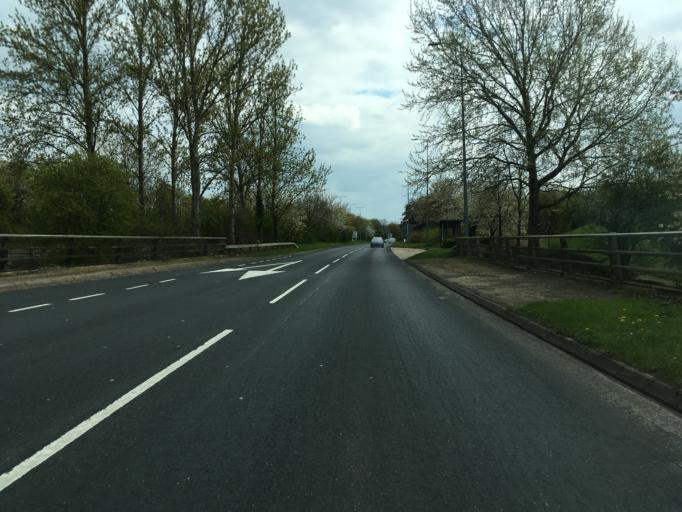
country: GB
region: England
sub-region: Milton Keynes
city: Milton Keynes
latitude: 52.0584
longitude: -0.7557
